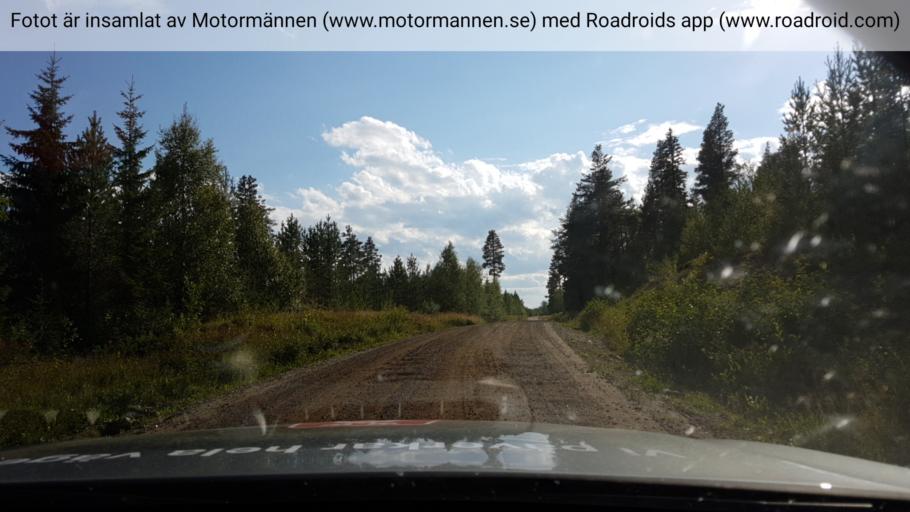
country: SE
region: Jaemtland
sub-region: Stroemsunds Kommun
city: Stroemsund
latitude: 63.7256
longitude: 16.0987
